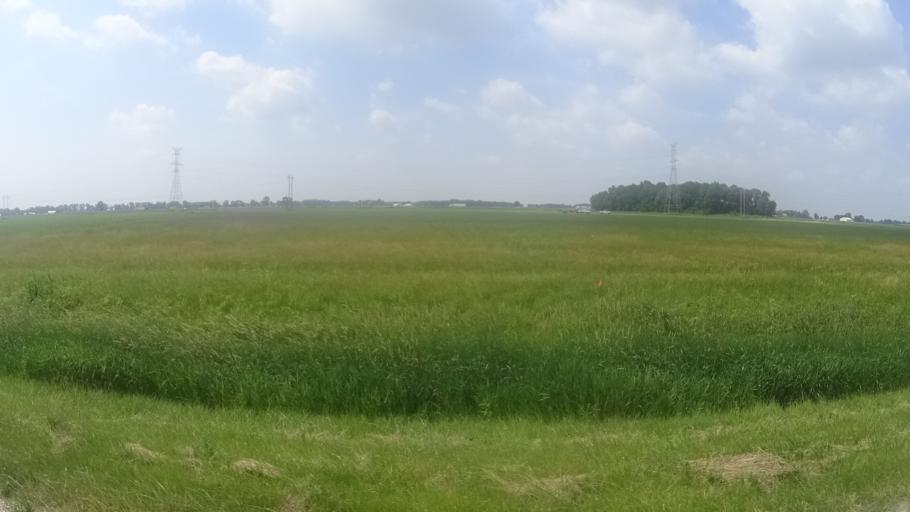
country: US
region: Ohio
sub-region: Erie County
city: Milan
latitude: 41.3379
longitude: -82.6591
